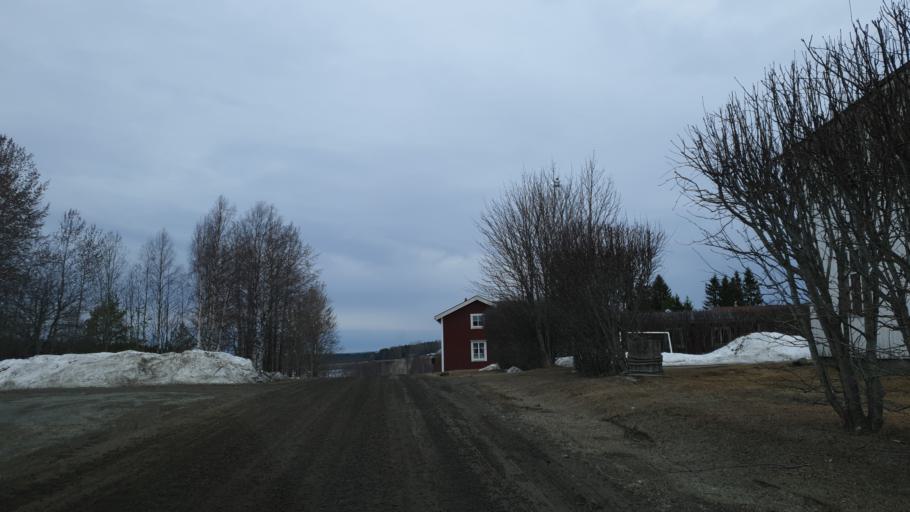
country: SE
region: Vaesterbotten
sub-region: Skelleftea Kommun
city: Burea
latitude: 64.3345
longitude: 21.1327
